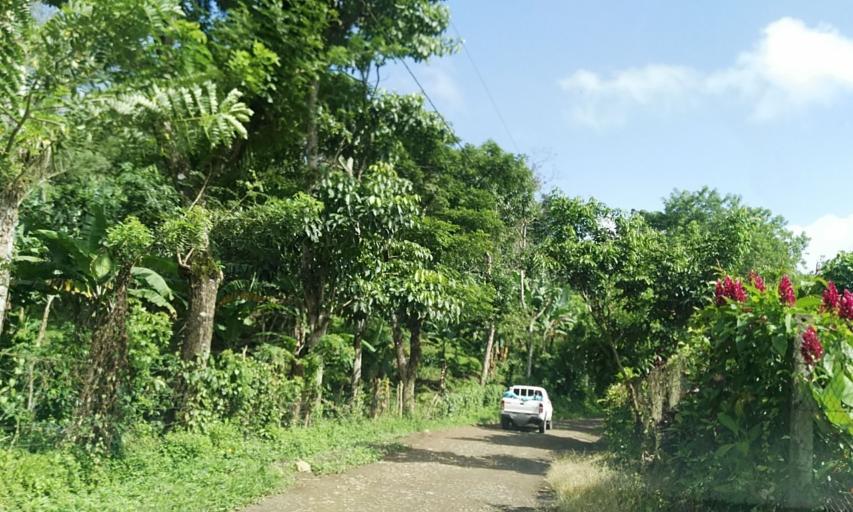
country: NI
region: Matagalpa
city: San Ramon
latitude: 12.9880
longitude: -85.8554
